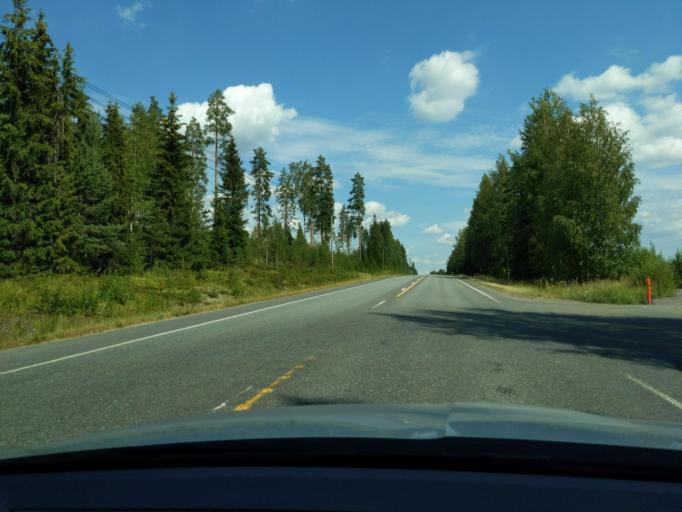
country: FI
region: Uusimaa
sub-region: Helsinki
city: Maentsaelae
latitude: 60.5595
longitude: 25.2068
